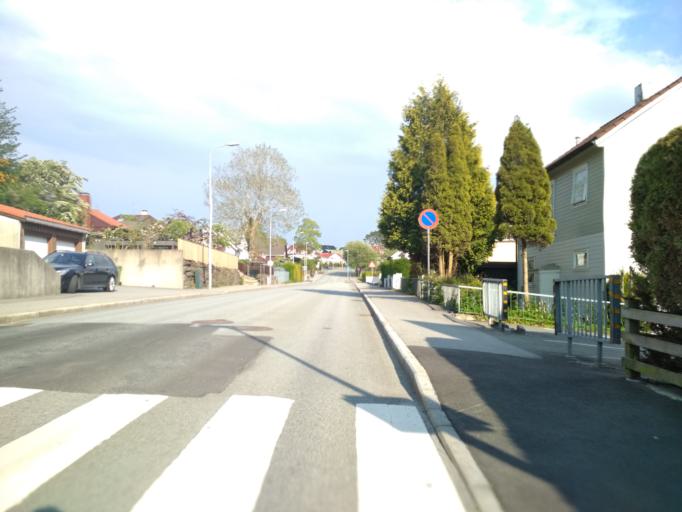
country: NO
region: Rogaland
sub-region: Stavanger
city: Stavanger
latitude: 58.9692
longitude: 5.7082
